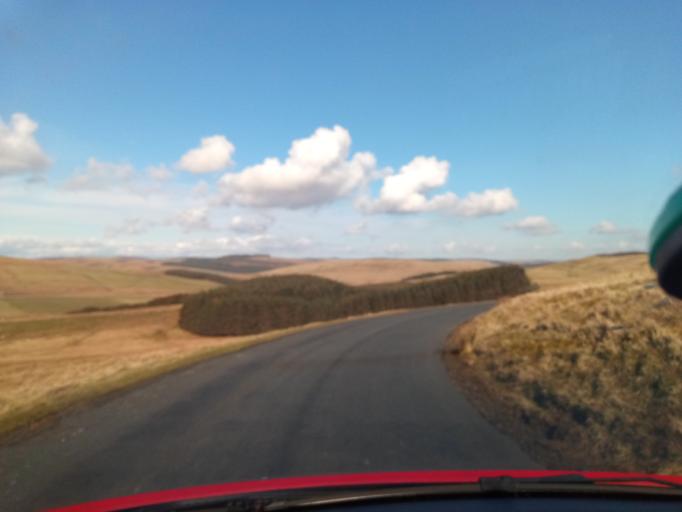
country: GB
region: Scotland
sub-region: The Scottish Borders
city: Hawick
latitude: 55.4469
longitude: -2.8881
